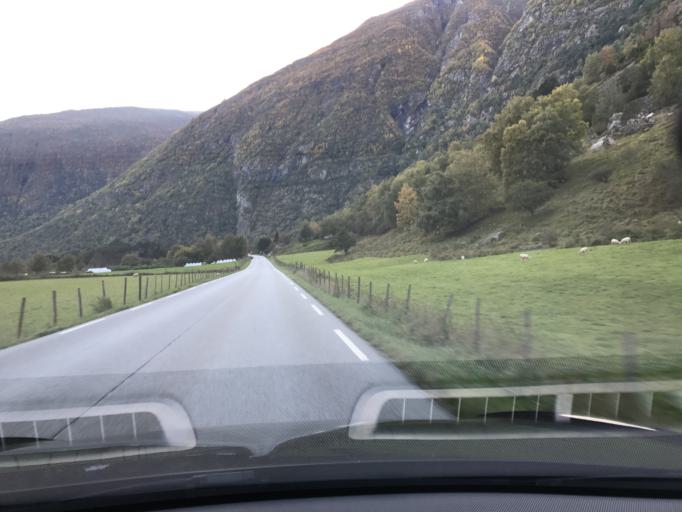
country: NO
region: Sogn og Fjordane
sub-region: Laerdal
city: Laerdalsoyri
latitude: 61.0800
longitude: 7.5053
